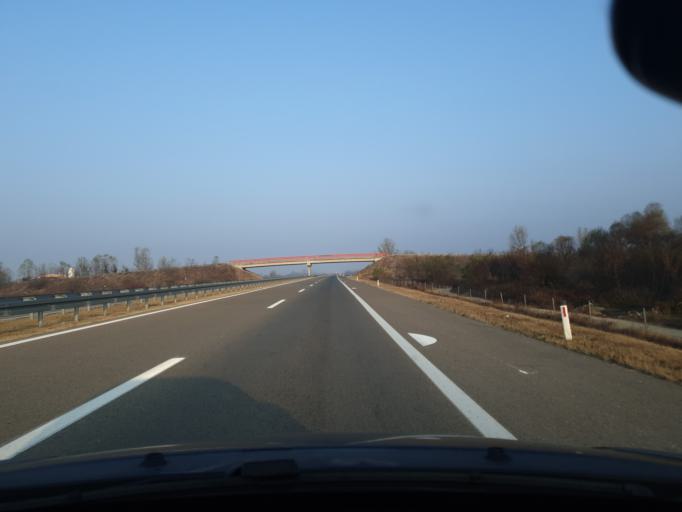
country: RS
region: Central Serbia
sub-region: Jablanicki Okrug
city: Leskovac
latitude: 43.0565
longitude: 21.9759
